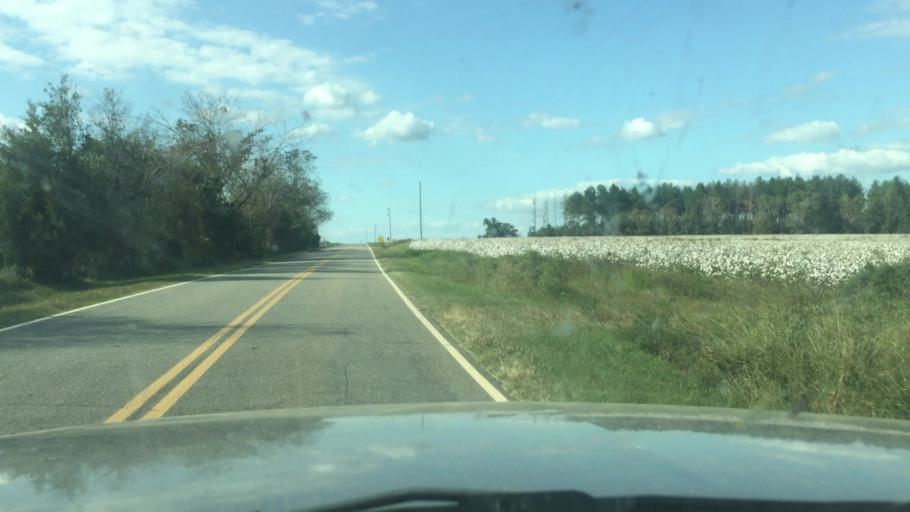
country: US
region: Georgia
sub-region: Terrell County
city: Dawson
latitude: 31.7560
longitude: -84.3500
